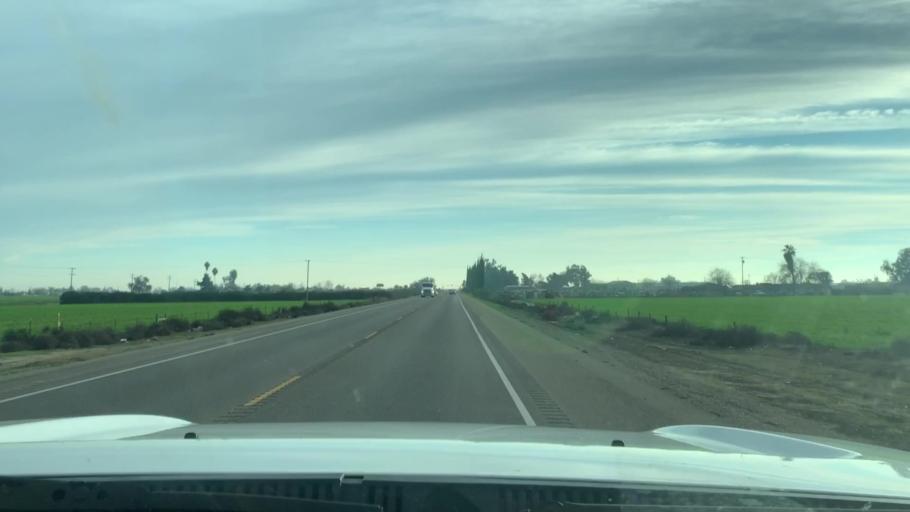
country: US
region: California
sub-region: Fresno County
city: Riverdale
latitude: 36.4402
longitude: -119.7994
